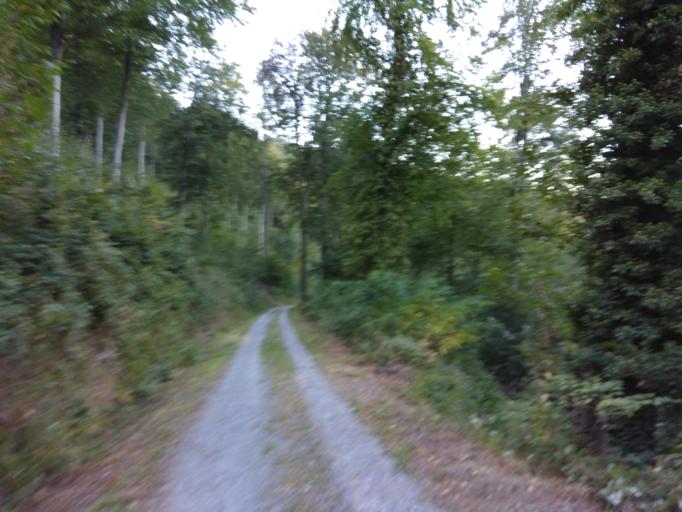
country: DE
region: Baden-Wuerttemberg
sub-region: Karlsruhe Region
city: Heidelberg
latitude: 49.4092
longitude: 8.7240
